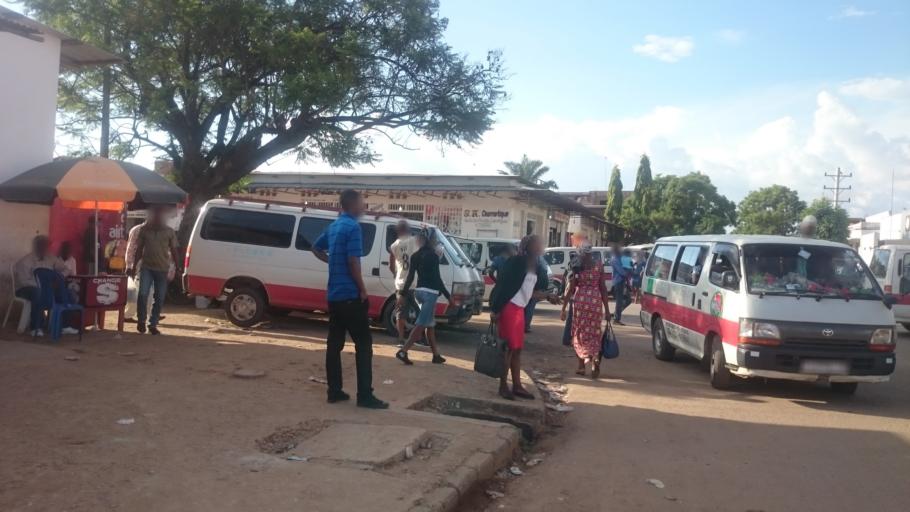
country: CD
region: Katanga
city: Lubumbashi
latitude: -11.6720
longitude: 27.4838
